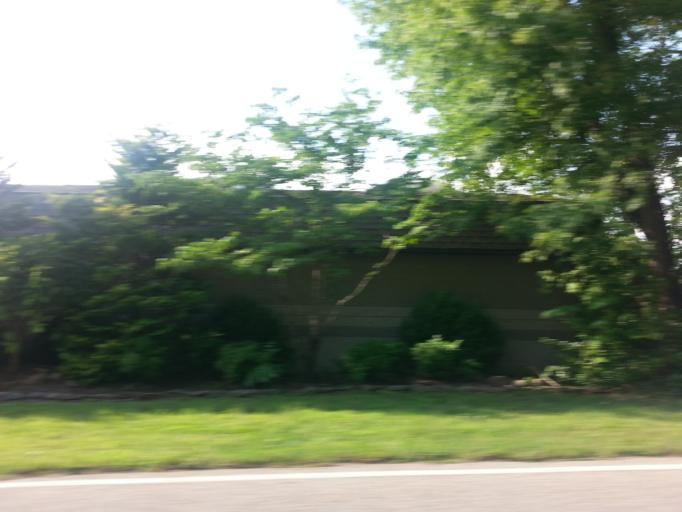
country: US
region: Tennessee
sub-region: Blount County
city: Louisville
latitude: 35.8222
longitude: -84.0475
